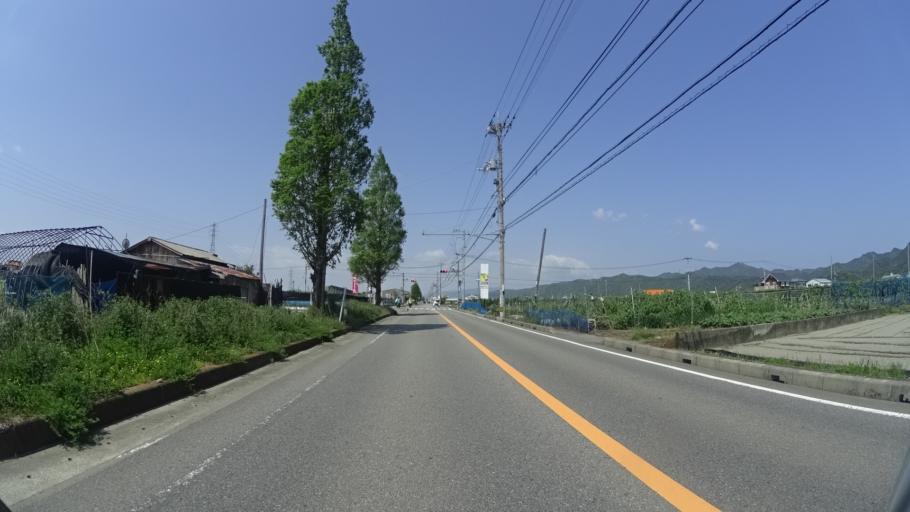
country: JP
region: Tokushima
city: Narutocho-mitsuishi
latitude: 34.1605
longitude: 134.5878
